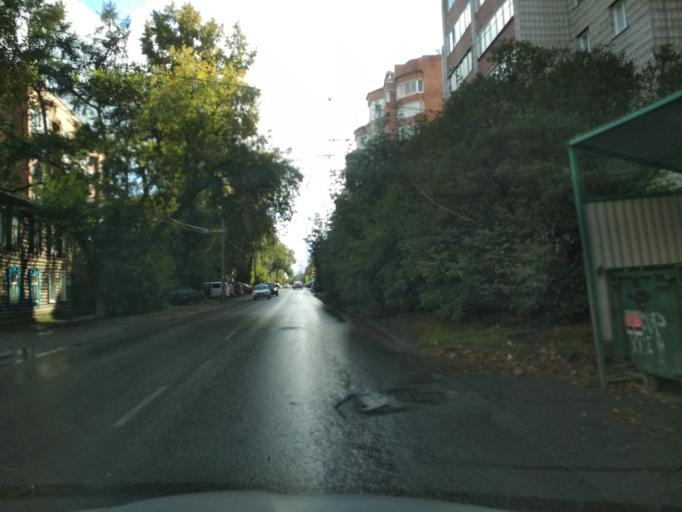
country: RU
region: Tomsk
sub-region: Tomskiy Rayon
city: Tomsk
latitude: 56.4753
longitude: 84.9758
